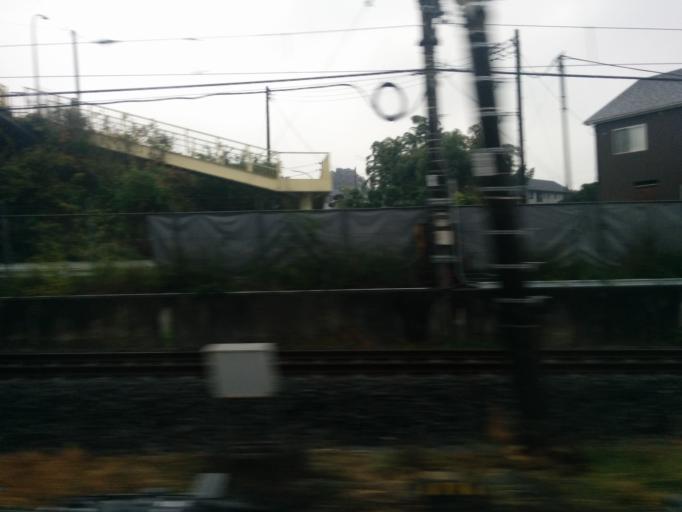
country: JP
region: Chiba
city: Sakura
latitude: 35.7103
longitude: 140.2308
